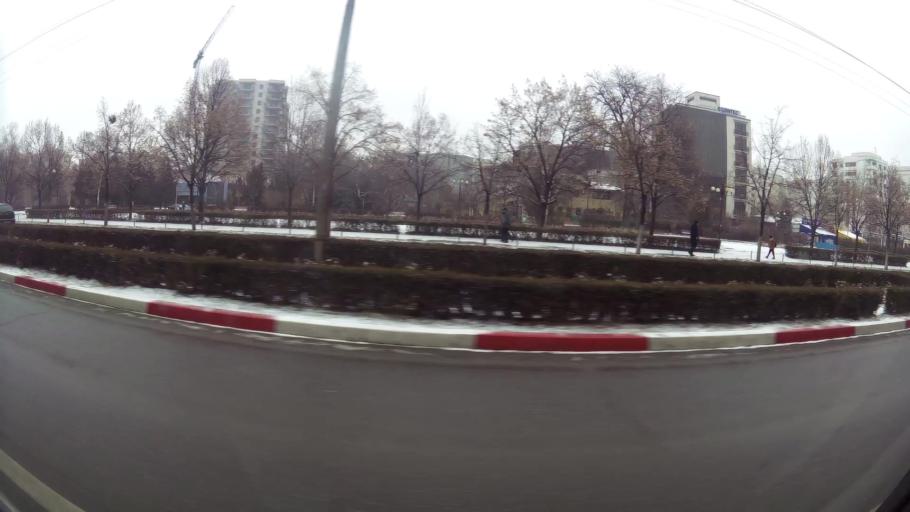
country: RO
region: Prahova
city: Ploiesti
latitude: 44.9446
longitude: 26.0148
